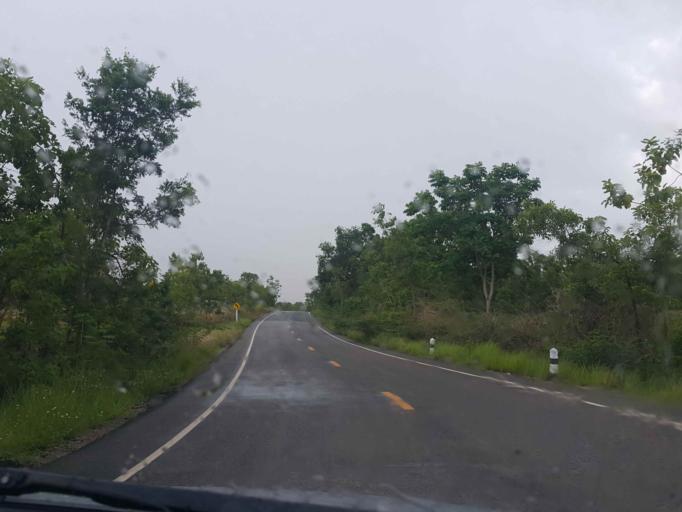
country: TH
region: Phayao
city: Dok Kham Tai
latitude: 19.0303
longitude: 99.9641
